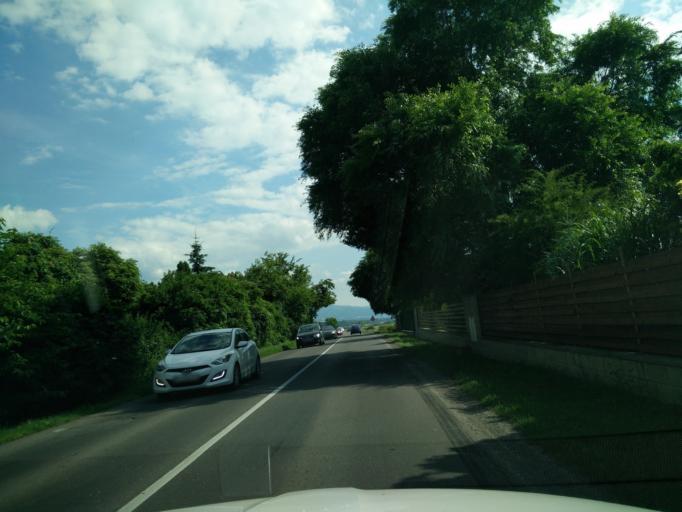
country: SK
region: Nitriansky
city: Prievidza
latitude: 48.8137
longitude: 18.6428
